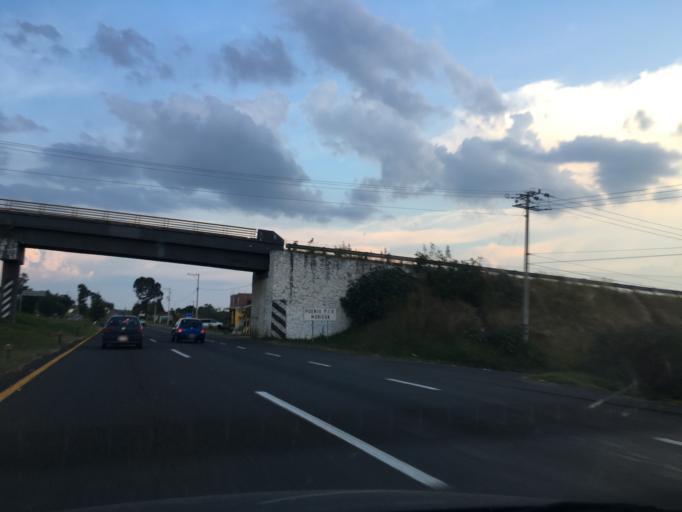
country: MX
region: Michoacan
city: Acuitzio del Canje
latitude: 19.5640
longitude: -101.3265
